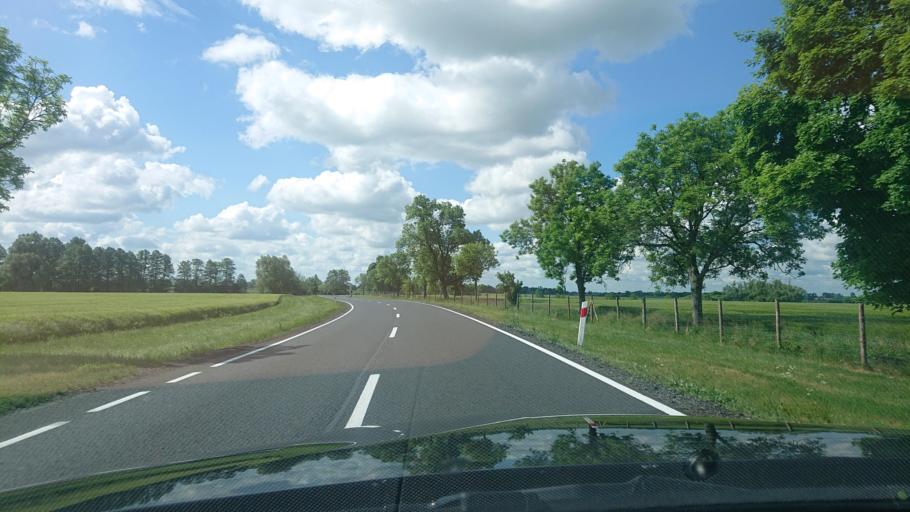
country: PL
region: Lower Silesian Voivodeship
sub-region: Powiat polkowicki
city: Radwanice
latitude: 51.5600
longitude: 15.9346
